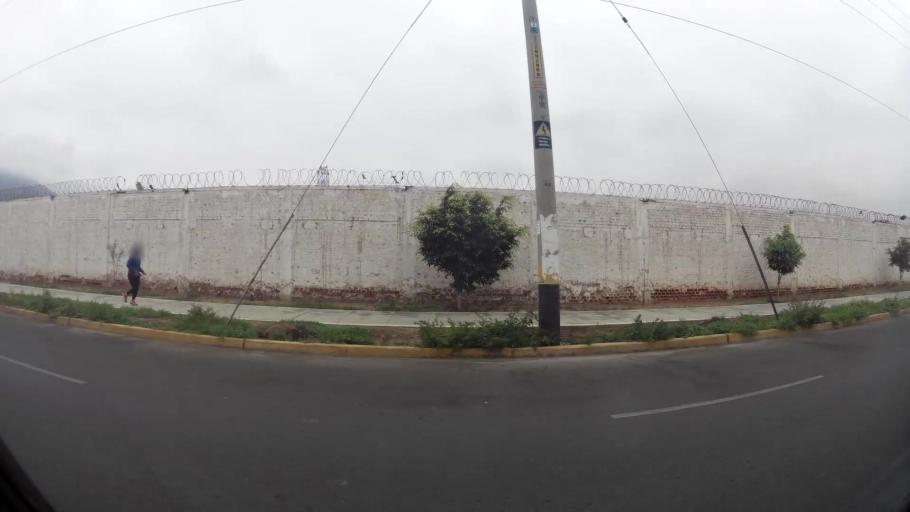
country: PE
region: Ancash
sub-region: Provincia de Santa
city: Chimbote
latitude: -9.0647
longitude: -78.5941
